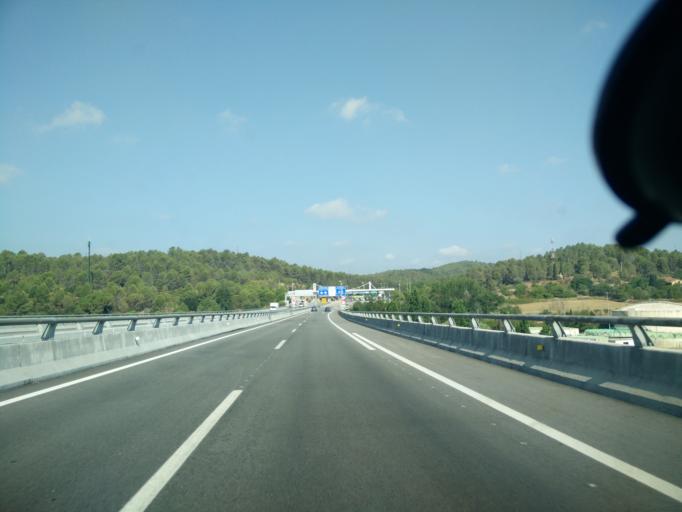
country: ES
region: Catalonia
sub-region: Provincia de Barcelona
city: Rubi
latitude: 41.5161
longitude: 2.0354
